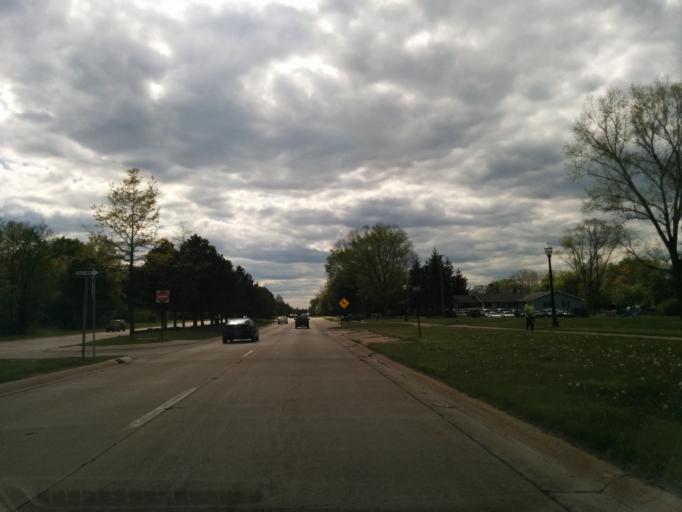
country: US
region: Michigan
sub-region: Oakland County
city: Farmington Hills
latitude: 42.4981
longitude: -83.4011
